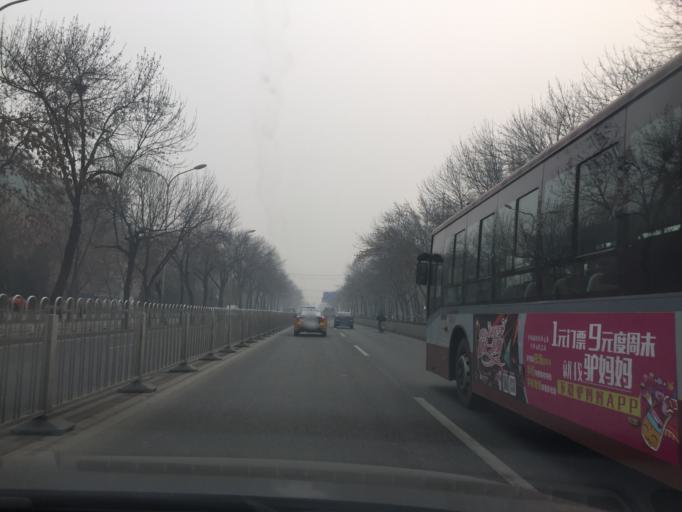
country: CN
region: Beijing
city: Qinghe
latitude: 40.0098
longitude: 116.3461
